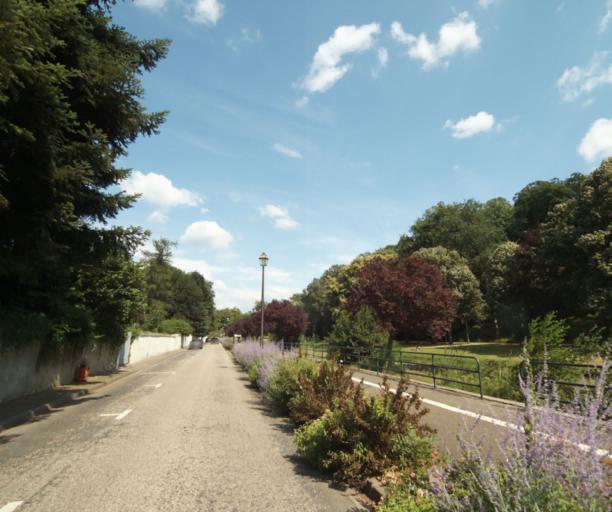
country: FR
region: Lorraine
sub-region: Departement de Meurthe-et-Moselle
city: Luneville
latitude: 48.5961
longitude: 6.4952
